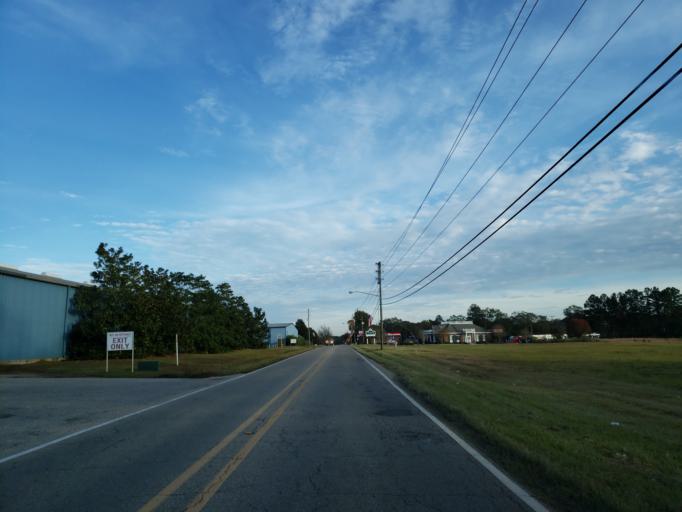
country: US
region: Mississippi
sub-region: Lamar County
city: Purvis
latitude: 31.1551
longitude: -89.4164
